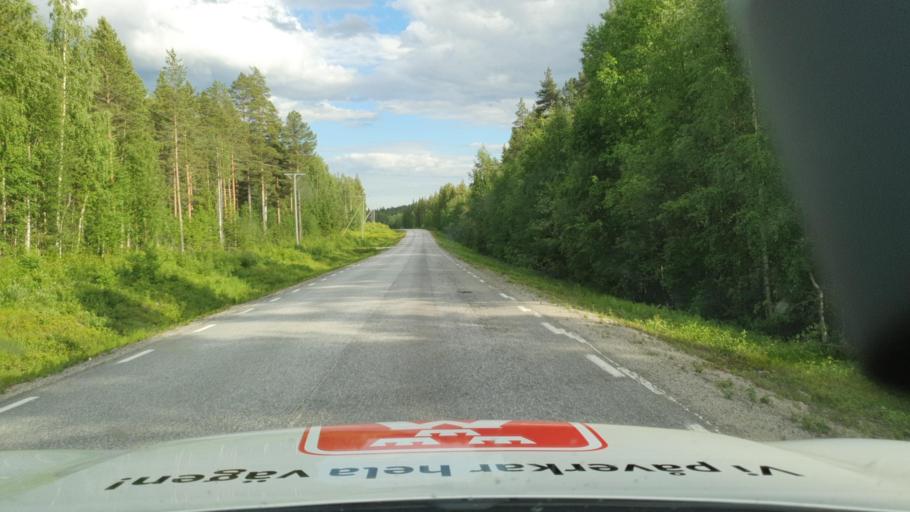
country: SE
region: Vaesterbotten
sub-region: Vindelns Kommun
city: Vindeln
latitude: 64.3967
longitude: 19.6681
